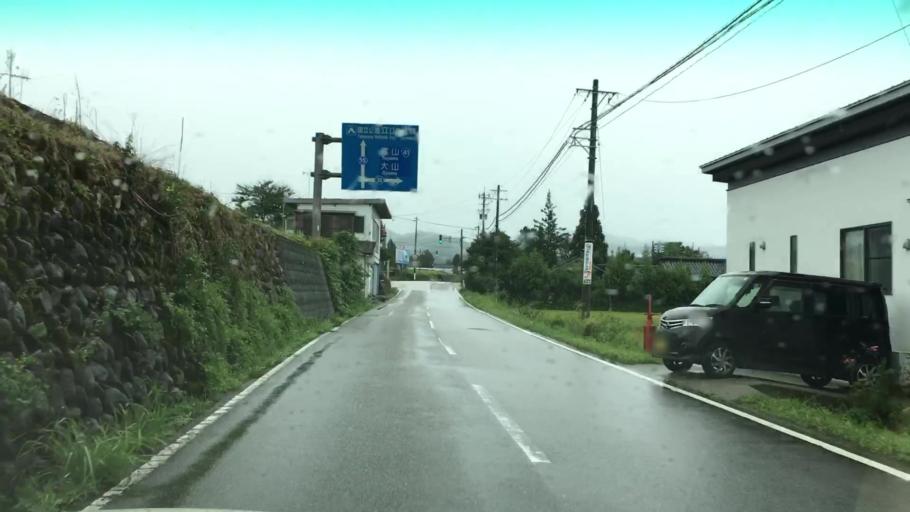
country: JP
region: Toyama
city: Kamiichi
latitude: 36.6126
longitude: 137.3218
